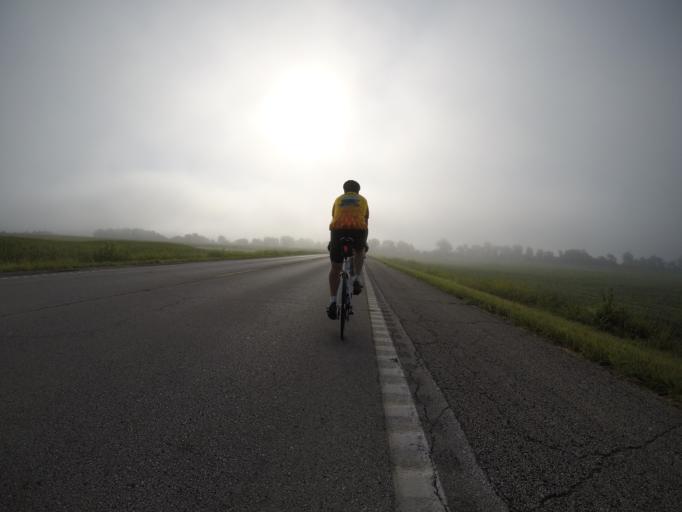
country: US
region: Kansas
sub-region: Leavenworth County
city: Leavenworth
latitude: 39.3259
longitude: -94.8708
